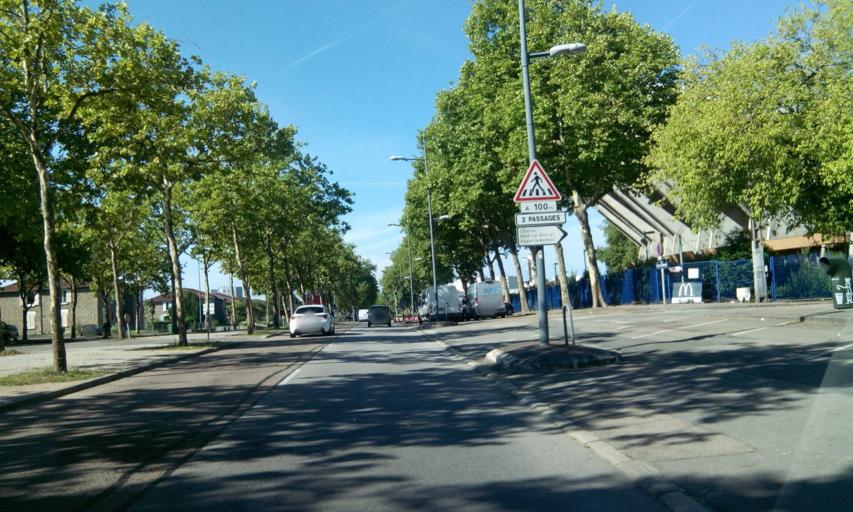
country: FR
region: Limousin
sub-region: Departement de la Haute-Vienne
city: Limoges
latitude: 45.8477
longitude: 1.2447
